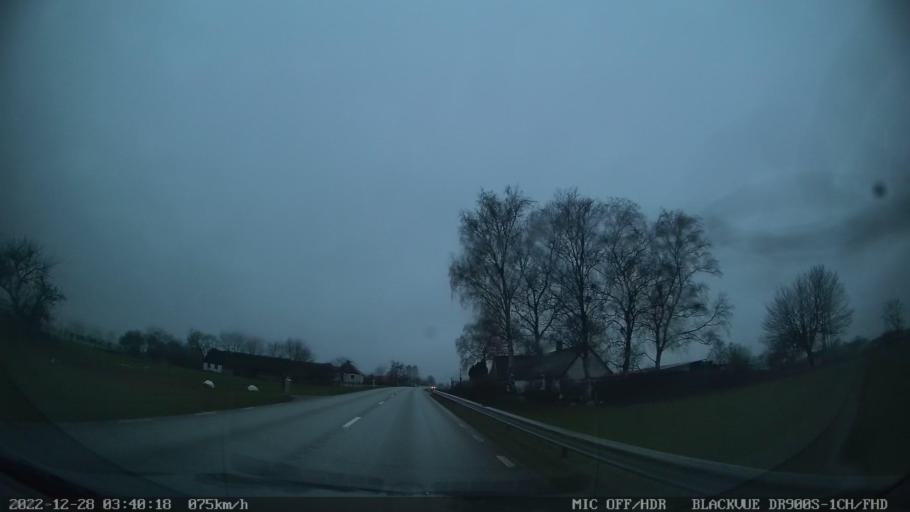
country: SE
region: Skane
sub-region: Tomelilla Kommun
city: Tomelilla
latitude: 55.5454
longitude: 14.0310
